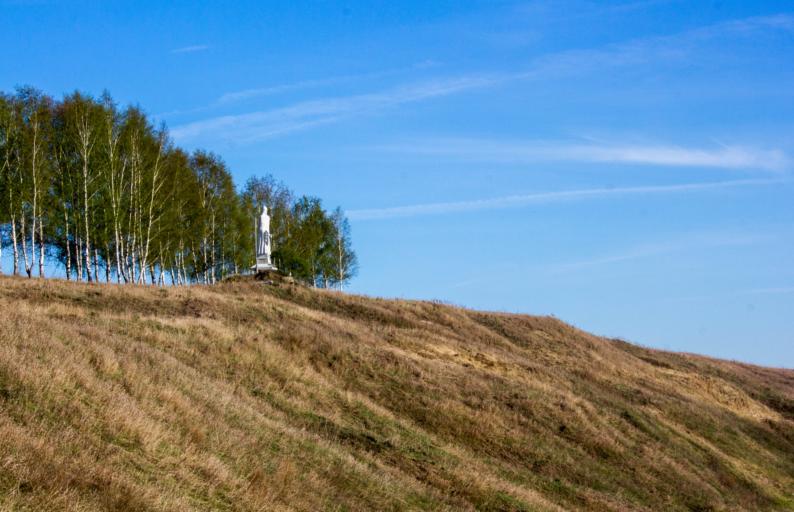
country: RU
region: Nizjnij Novgorod
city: Dal'neye Konstantinovo
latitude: 55.8943
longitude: 44.1534
